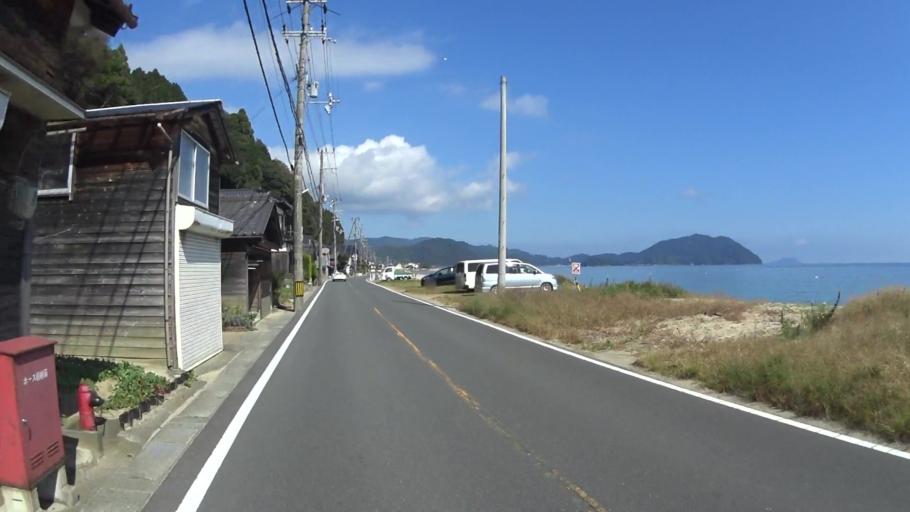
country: JP
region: Kyoto
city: Miyazu
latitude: 35.6500
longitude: 135.2535
